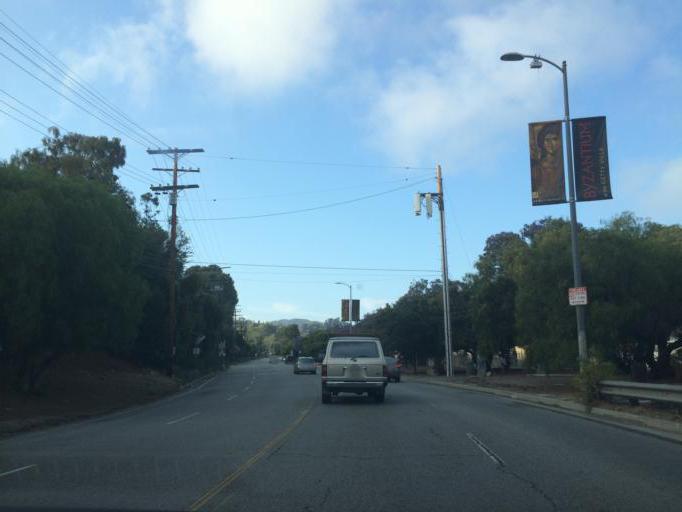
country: US
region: California
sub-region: Los Angeles County
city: Santa Monica
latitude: 34.0563
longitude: -118.4962
